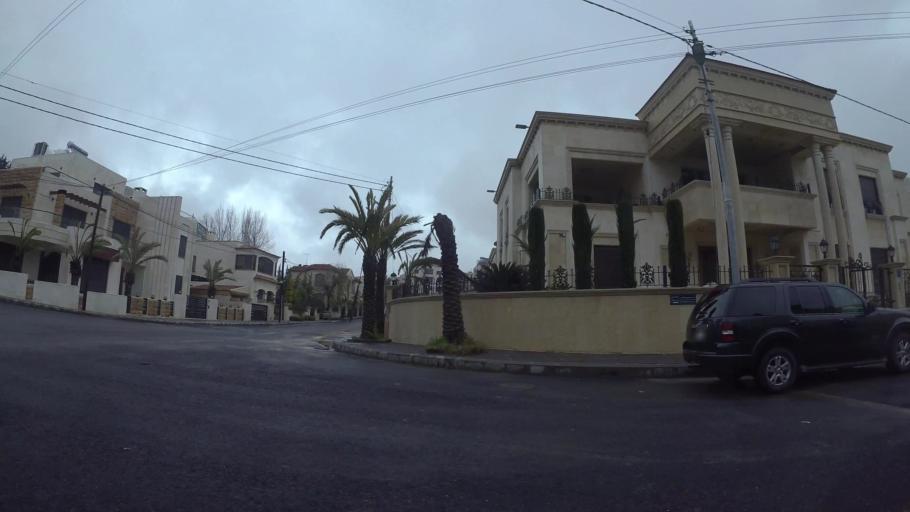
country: JO
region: Amman
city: Al Jubayhah
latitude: 32.0036
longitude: 35.8191
